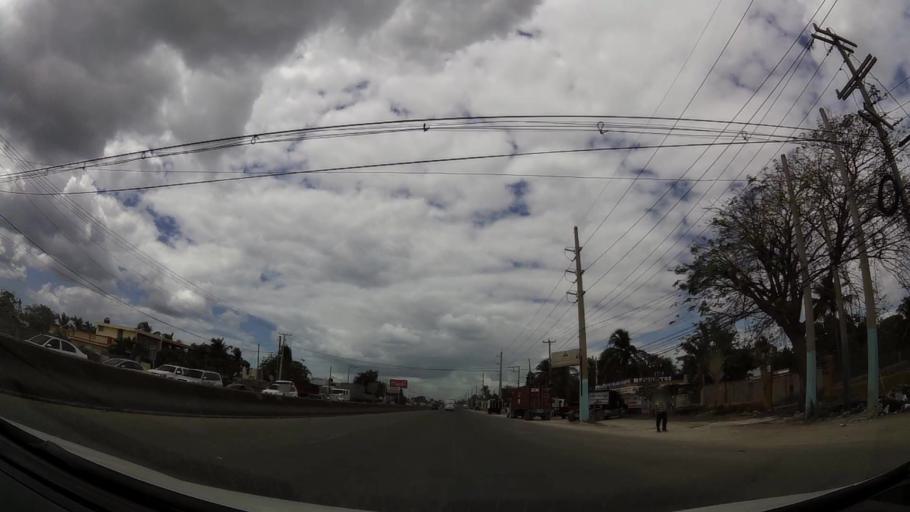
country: DO
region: Santo Domingo
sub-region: Santo Domingo
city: Boca Chica
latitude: 18.4491
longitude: -69.6580
